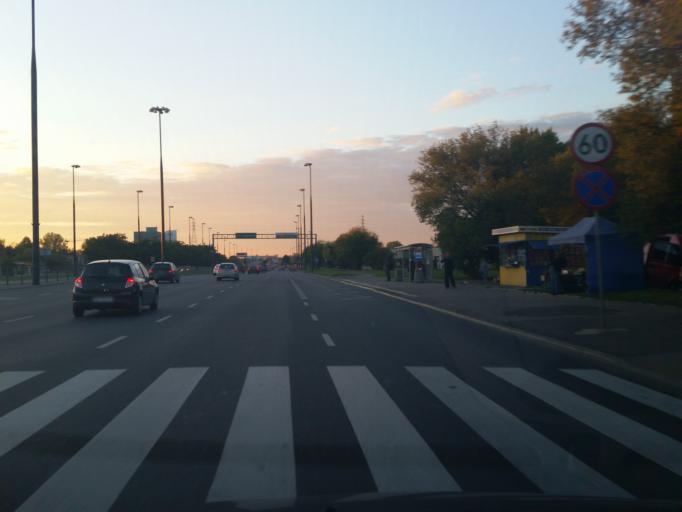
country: PL
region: Masovian Voivodeship
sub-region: Warszawa
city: Bialoleka
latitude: 52.3037
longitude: 20.9891
